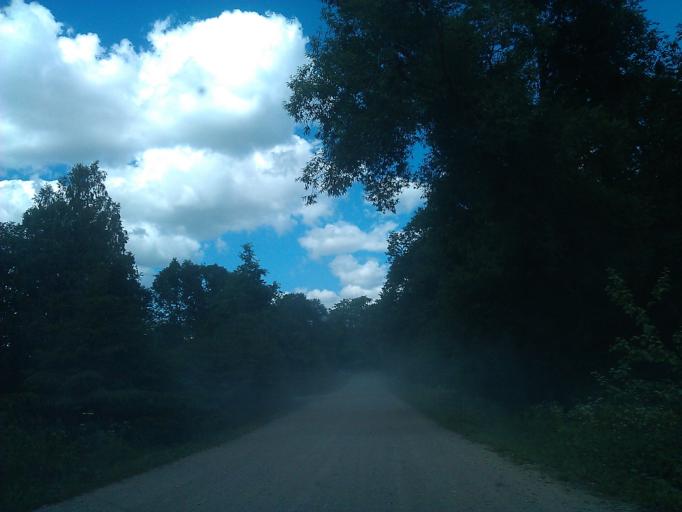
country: LV
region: Vilanu
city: Vilani
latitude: 56.5882
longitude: 26.9512
